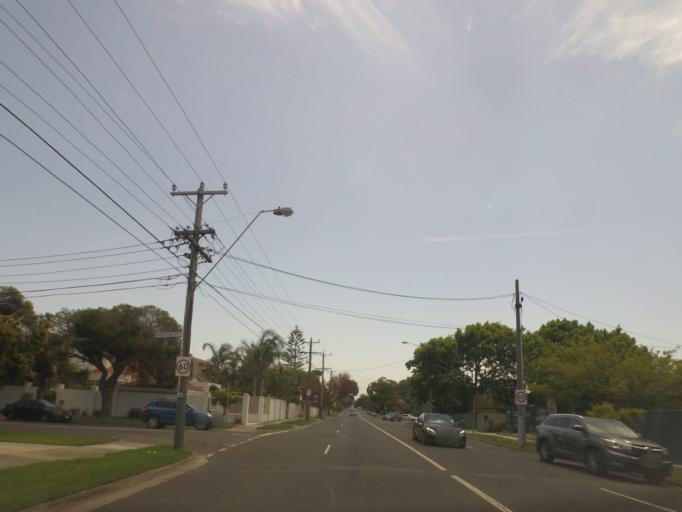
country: AU
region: Victoria
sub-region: Bayside
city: Black Rock
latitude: -37.9677
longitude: 145.0177
